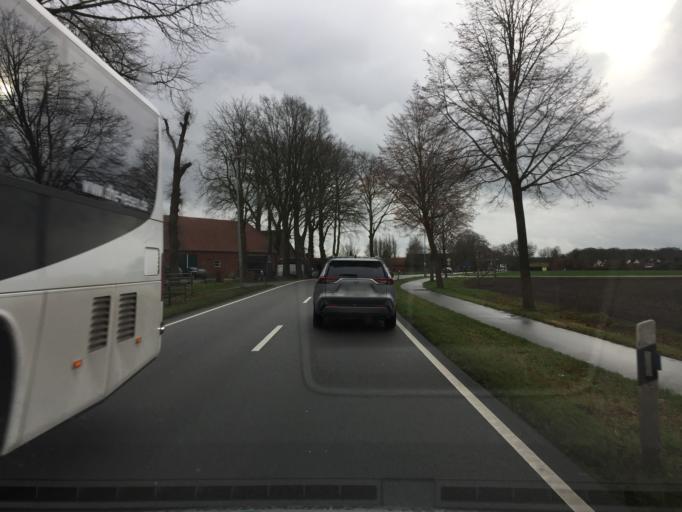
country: DE
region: Lower Saxony
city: Stuhr
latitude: 52.9934
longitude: 8.7178
